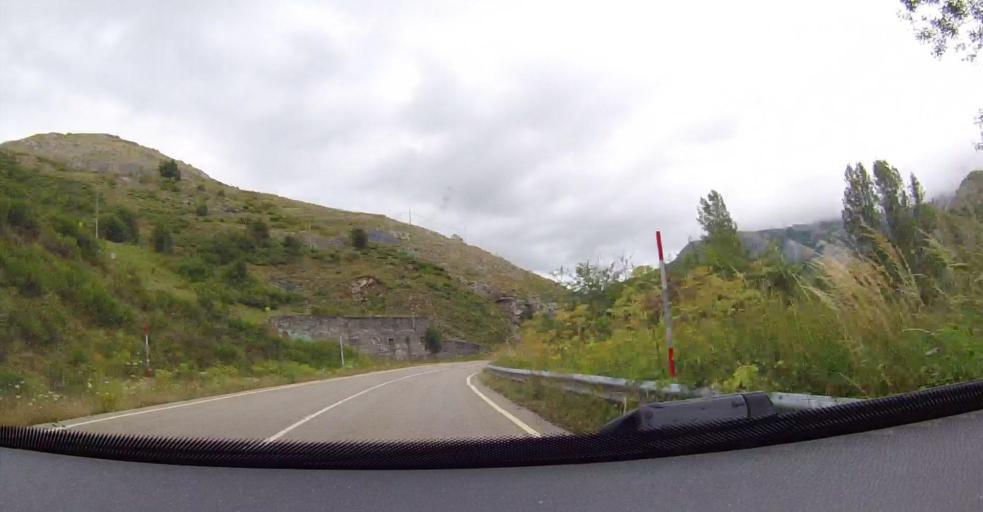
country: ES
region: Castille and Leon
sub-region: Provincia de Leon
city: Buron
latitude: 43.0281
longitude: -5.0652
